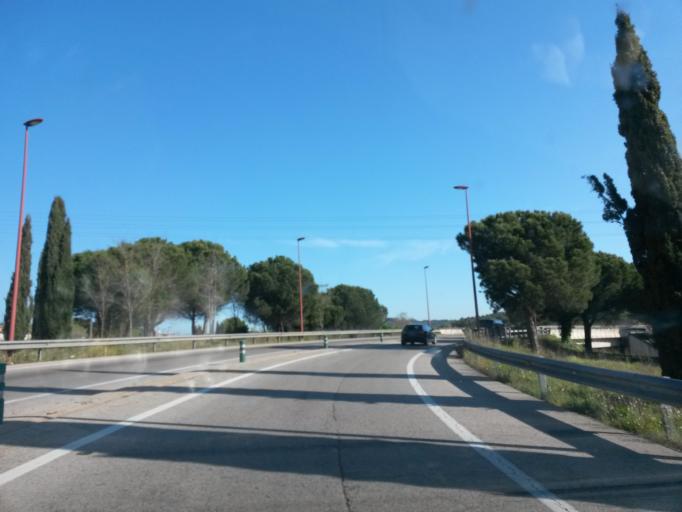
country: ES
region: Catalonia
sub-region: Provincia de Girona
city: Sarria de Ter
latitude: 42.0317
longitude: 2.8257
